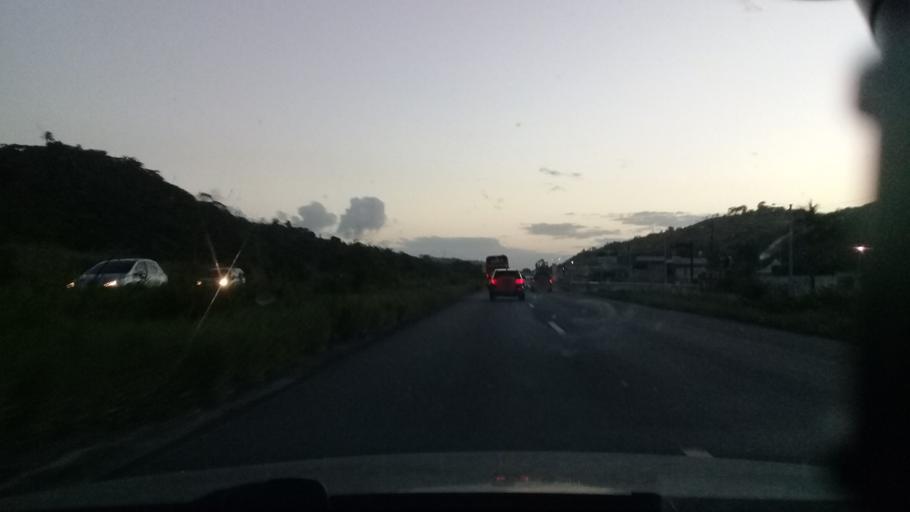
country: BR
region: Pernambuco
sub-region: Vitoria De Santo Antao
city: Vitoria de Santo Antao
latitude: -8.1117
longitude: -35.2047
